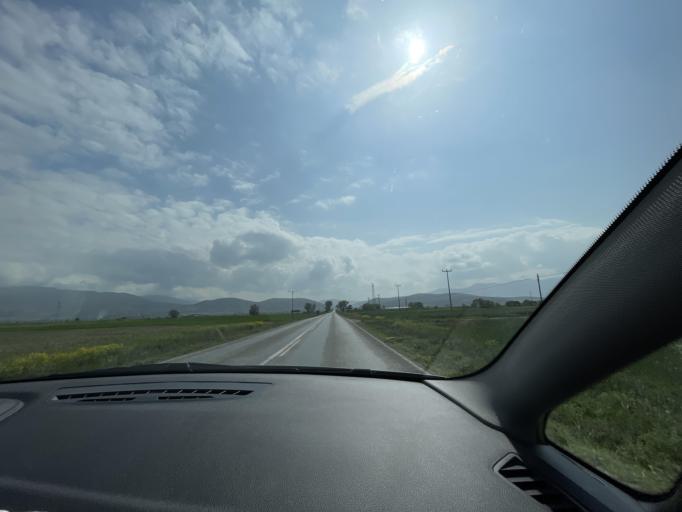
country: TR
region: Denizli
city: Acipayam
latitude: 37.5085
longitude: 29.4092
